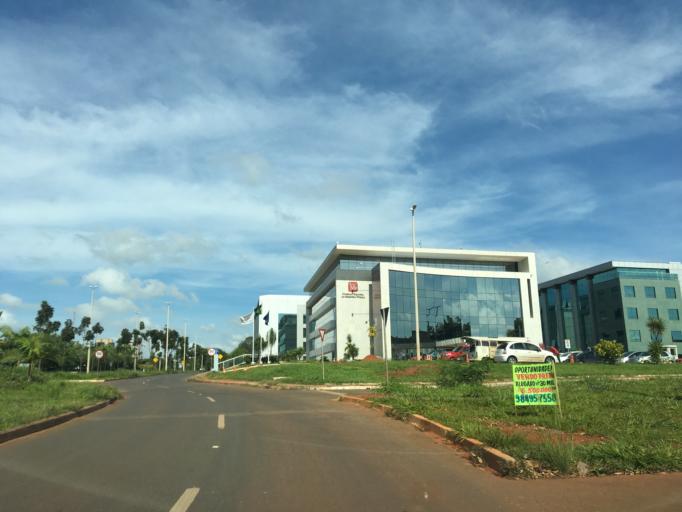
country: BR
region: Federal District
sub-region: Brasilia
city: Brasilia
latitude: -15.8051
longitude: -47.8674
